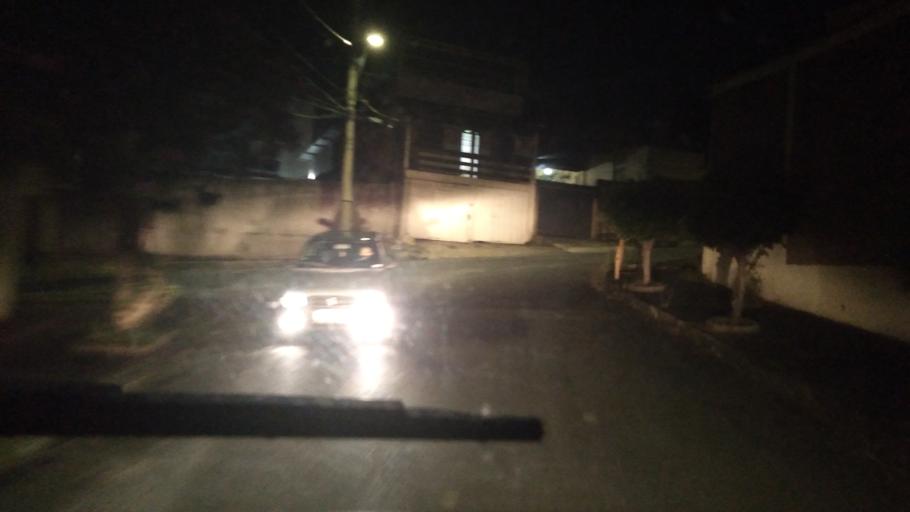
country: BR
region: Minas Gerais
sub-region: Belo Horizonte
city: Belo Horizonte
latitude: -19.8747
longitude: -43.9477
